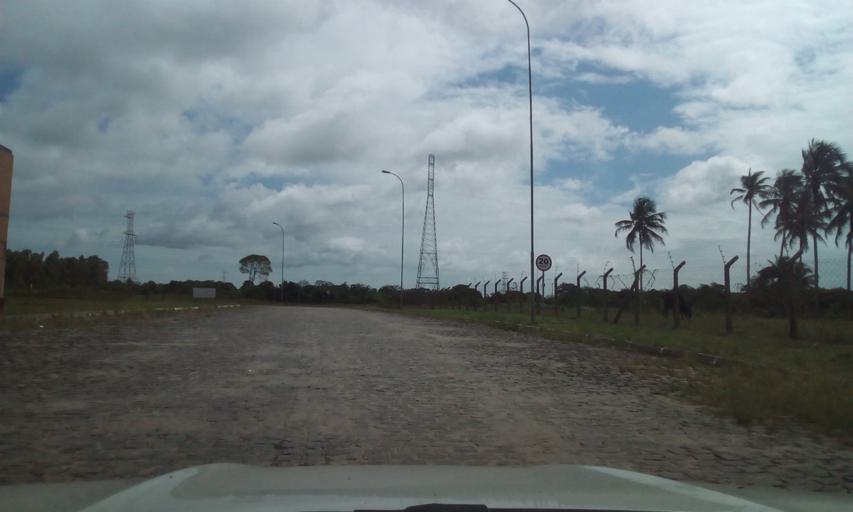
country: BR
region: Paraiba
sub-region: Conde
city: Conde
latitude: -7.1911
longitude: -34.8952
